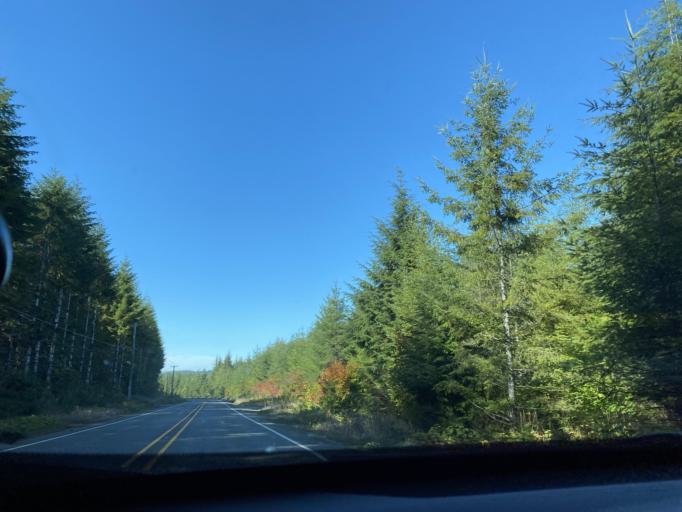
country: US
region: Washington
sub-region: Clallam County
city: Forks
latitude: 47.9642
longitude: -124.4361
